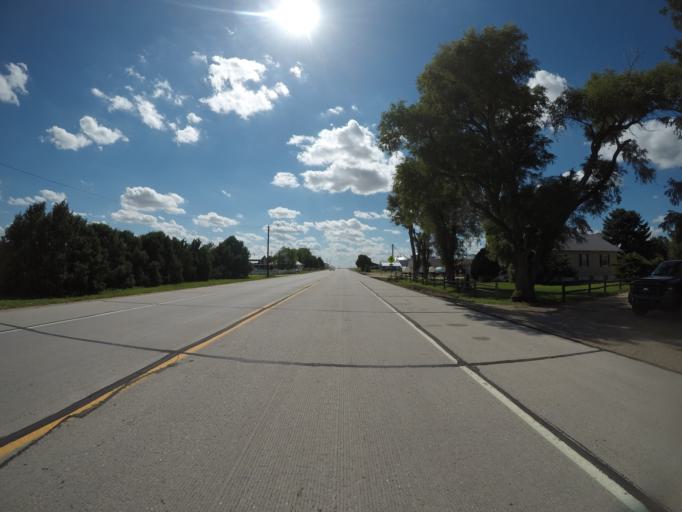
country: US
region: Colorado
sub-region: Phillips County
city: Holyoke
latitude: 40.6117
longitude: -102.4701
